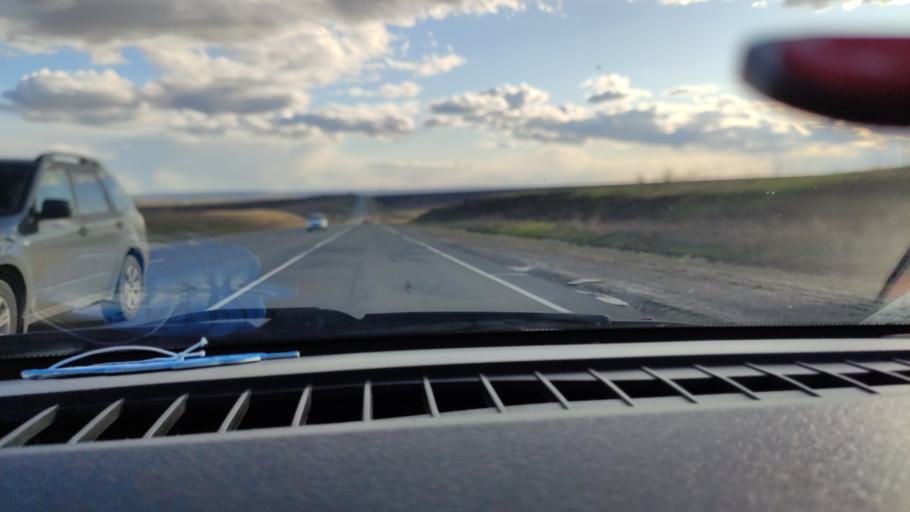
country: RU
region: Saratov
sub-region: Saratovskiy Rayon
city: Saratov
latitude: 51.7558
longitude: 46.0657
